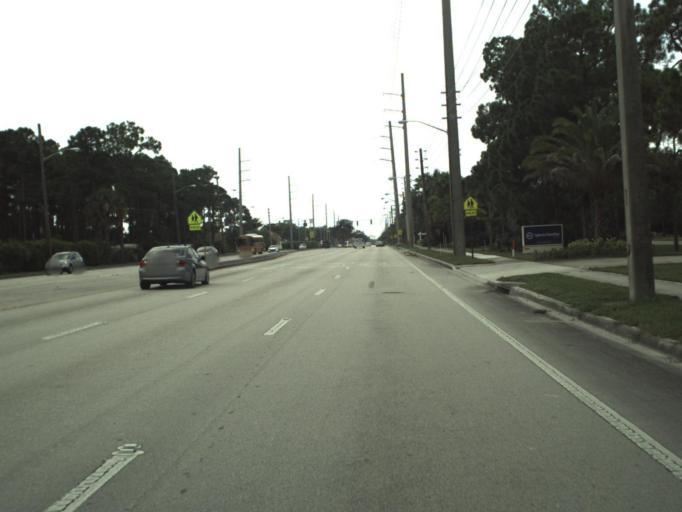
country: US
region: Florida
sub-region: Palm Beach County
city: Royal Palm Estates
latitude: 26.6656
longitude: -80.1453
